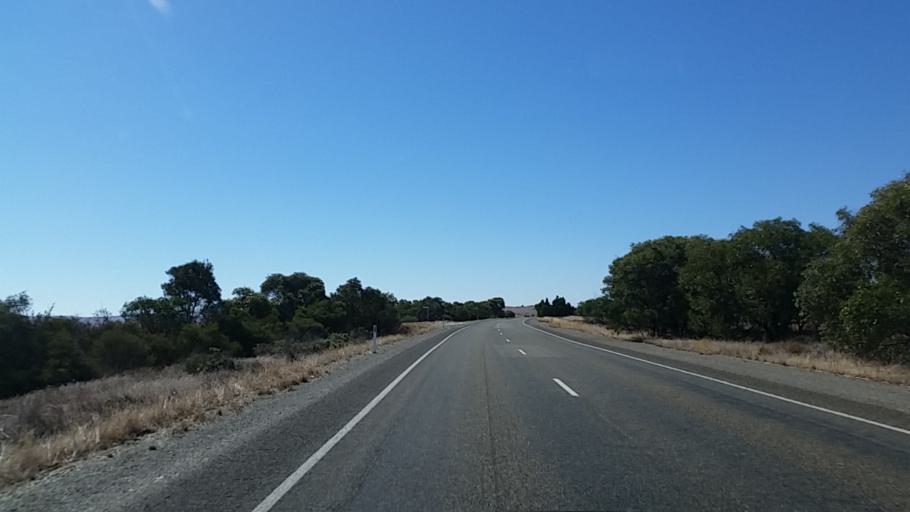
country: AU
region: South Australia
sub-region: Northern Areas
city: Jamestown
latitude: -33.2442
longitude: 138.8744
